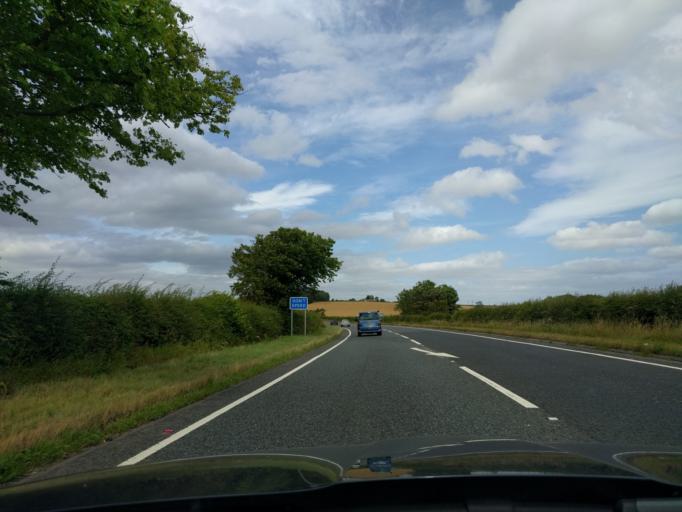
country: GB
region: England
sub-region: Northumberland
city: Felton
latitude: 55.2544
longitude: -1.7022
